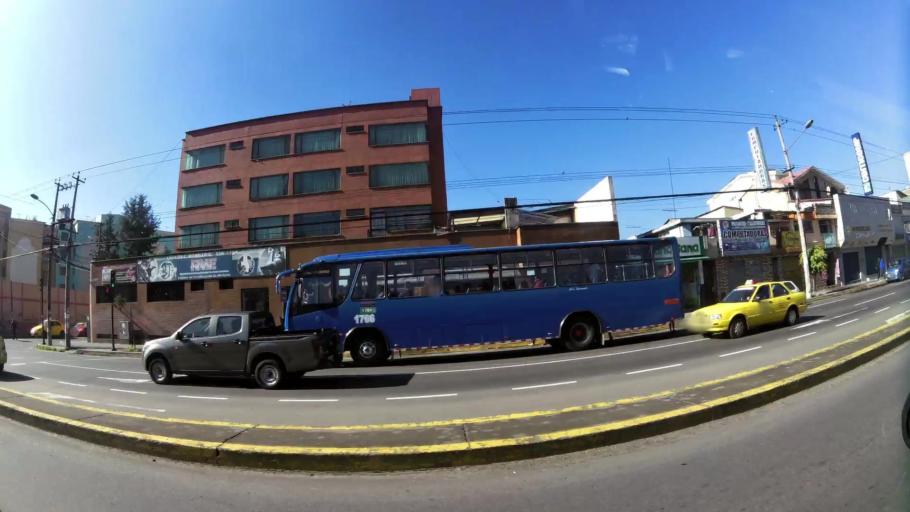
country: EC
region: Pichincha
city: Quito
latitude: -0.2480
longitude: -78.5264
